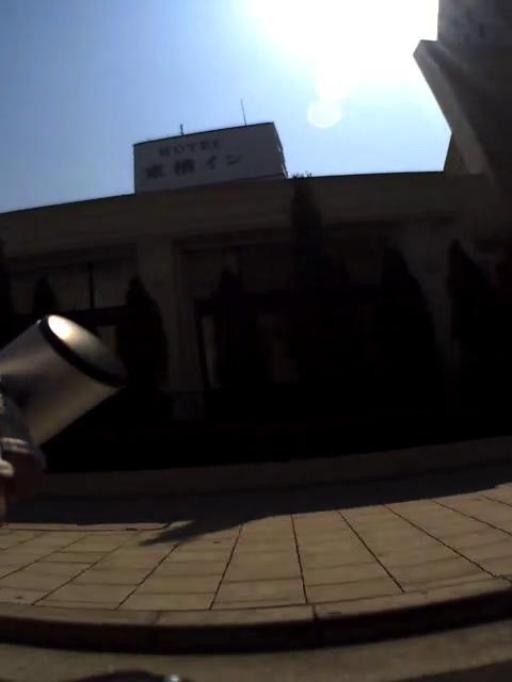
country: JP
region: Osaka
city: Osaka-shi
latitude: 34.6815
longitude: 135.5118
